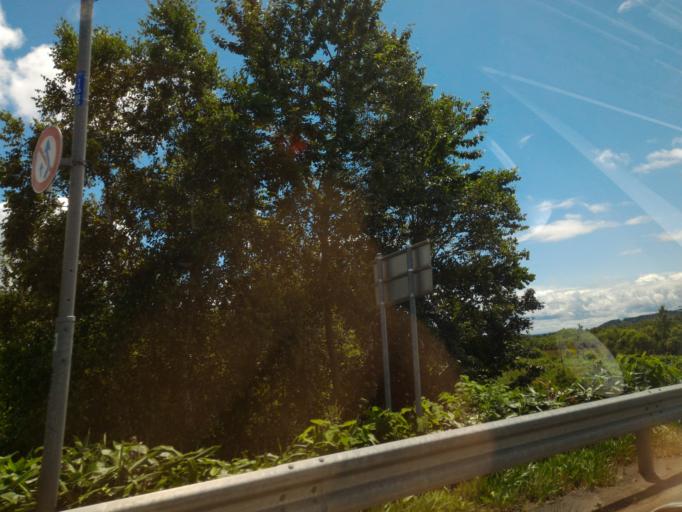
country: JP
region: Hokkaido
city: Nayoro
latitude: 44.5951
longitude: 142.3104
